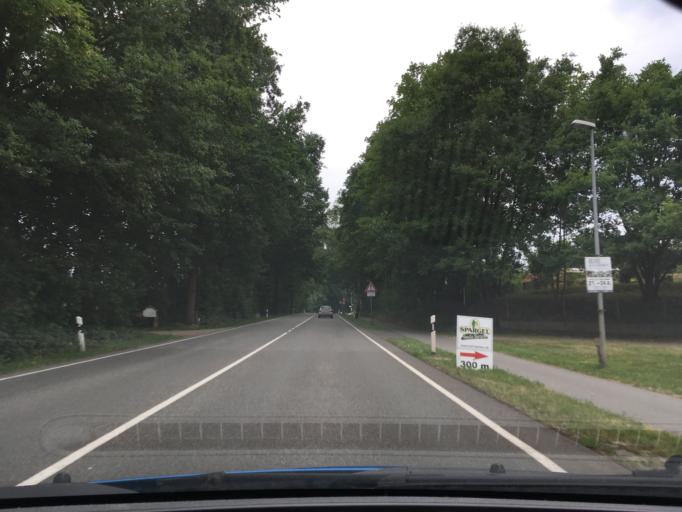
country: DE
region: Lower Saxony
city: Wenzendorf
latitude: 53.3838
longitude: 9.7987
